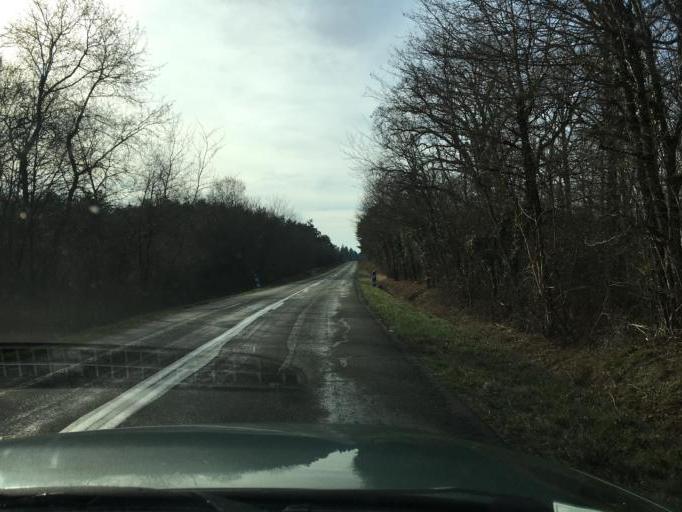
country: FR
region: Centre
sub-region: Departement du Loiret
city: Ligny-le-Ribault
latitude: 47.6890
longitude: 1.8138
